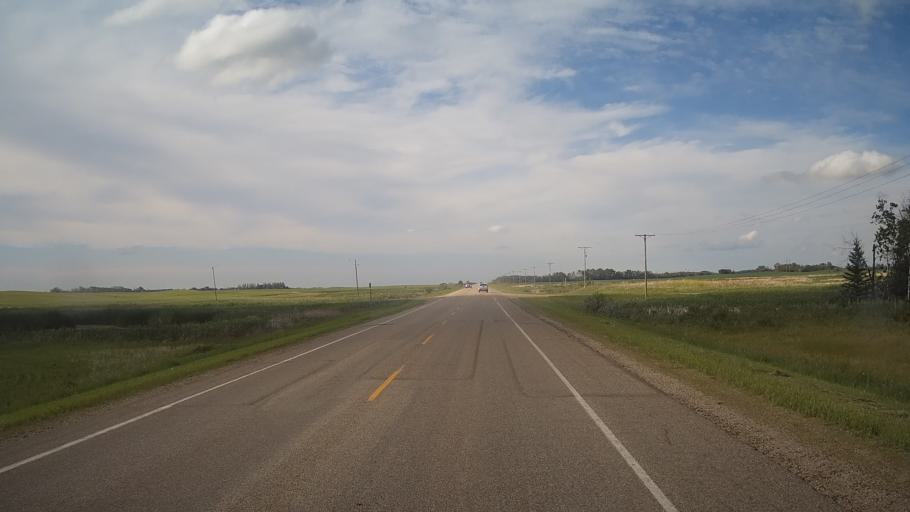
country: CA
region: Saskatchewan
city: Foam Lake
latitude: 51.6070
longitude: -103.8459
